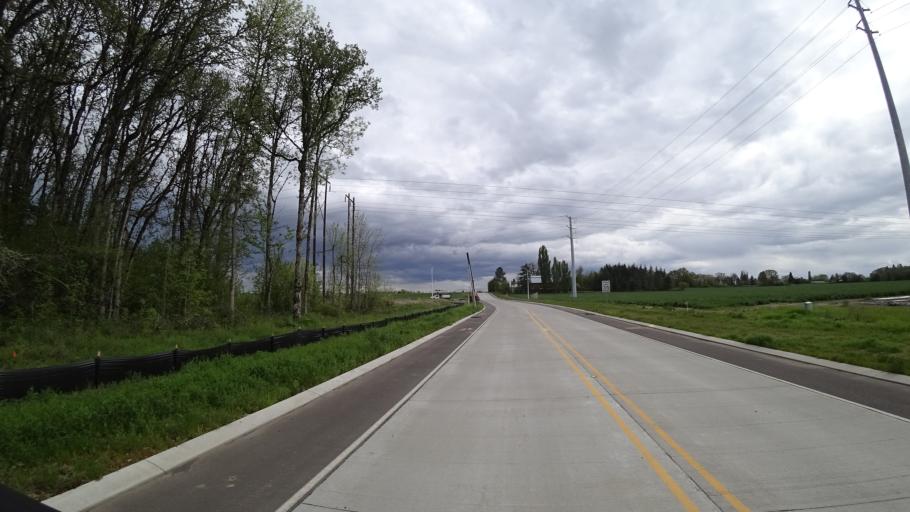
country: US
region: Oregon
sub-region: Washington County
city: Rockcreek
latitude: 45.5578
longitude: -122.9364
